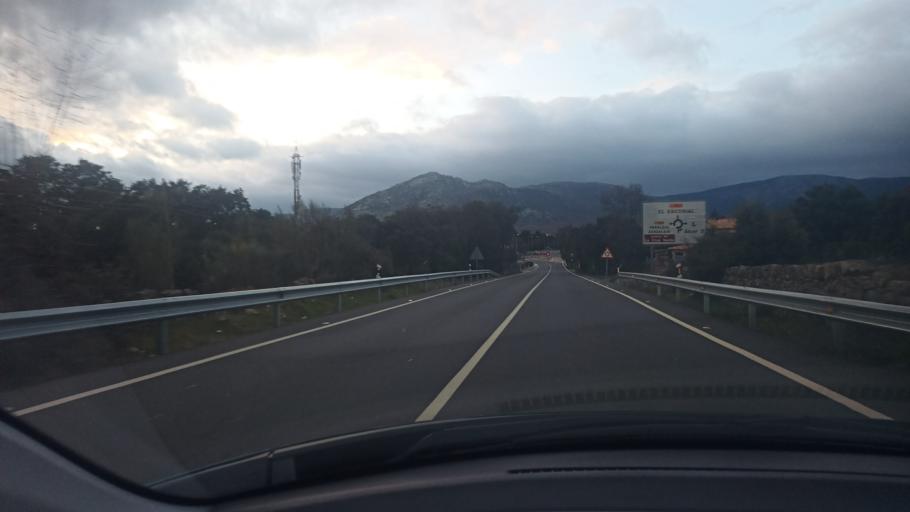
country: ES
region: Madrid
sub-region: Provincia de Madrid
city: El Escorial
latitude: 40.5434
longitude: -4.1077
